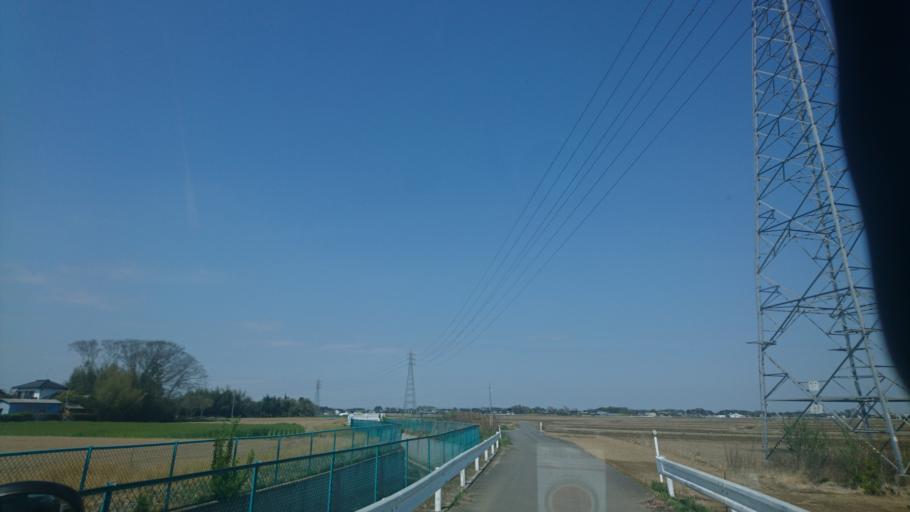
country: JP
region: Ibaraki
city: Ishige
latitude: 36.0855
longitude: 139.9754
